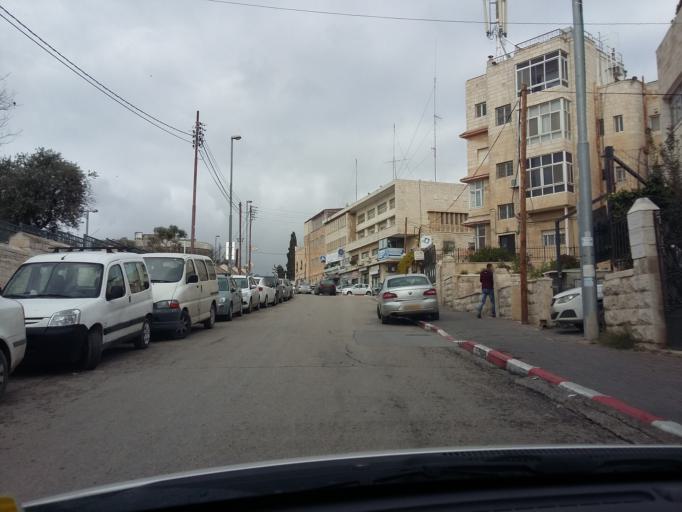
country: PS
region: West Bank
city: East Jerusalem
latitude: 31.7852
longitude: 35.2357
